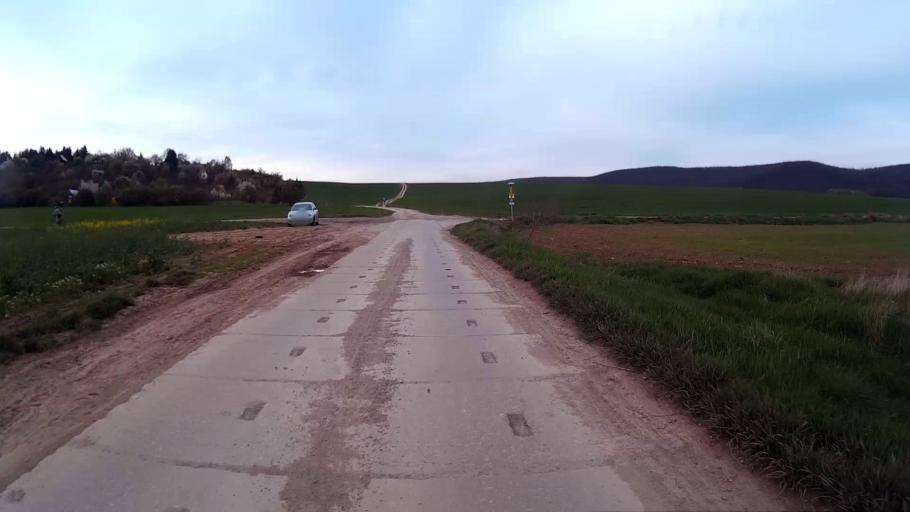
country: CZ
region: South Moravian
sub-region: Mesto Brno
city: Mokra Hora
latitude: 49.2407
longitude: 16.5457
